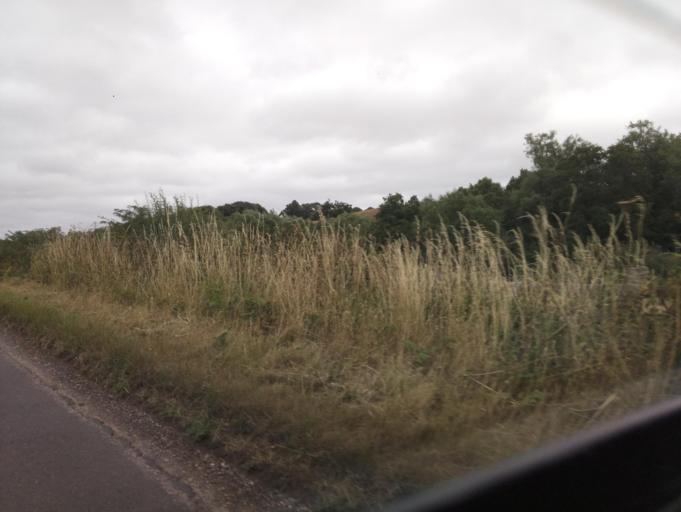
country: GB
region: England
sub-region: Derbyshire
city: Repton
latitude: 52.8178
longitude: -1.5405
